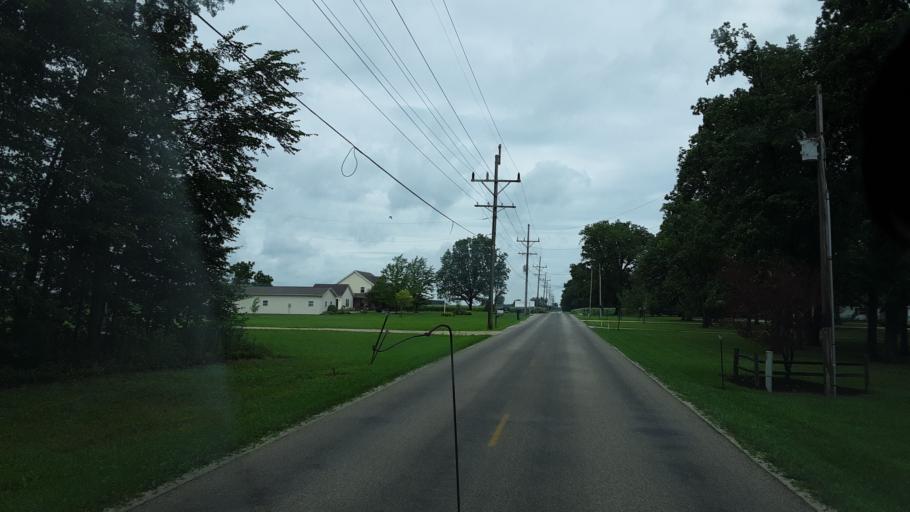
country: US
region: Indiana
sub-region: Jay County
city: Portland
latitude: 40.4602
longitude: -85.0202
